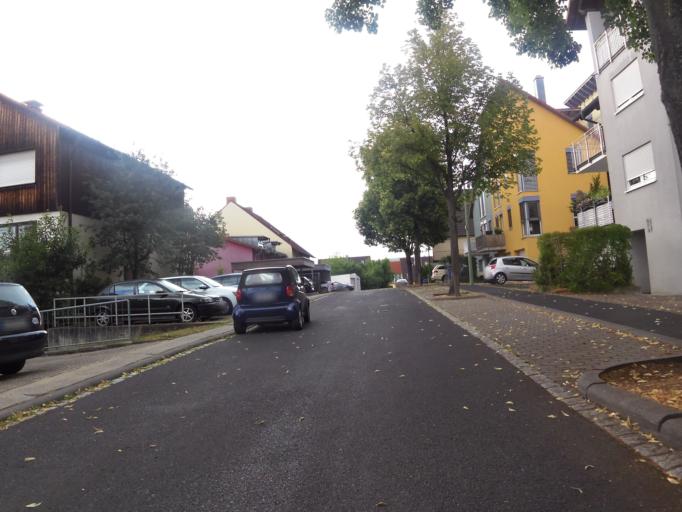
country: DE
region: Bavaria
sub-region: Regierungsbezirk Unterfranken
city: Wuerzburg
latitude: 49.8206
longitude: 9.9662
